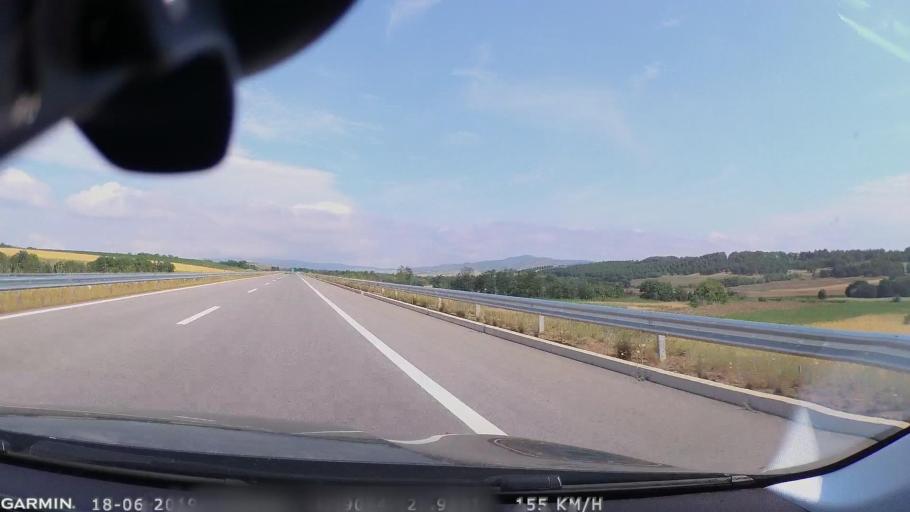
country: MK
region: Sveti Nikole
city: Gorobinci
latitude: 41.9055
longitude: 21.9088
